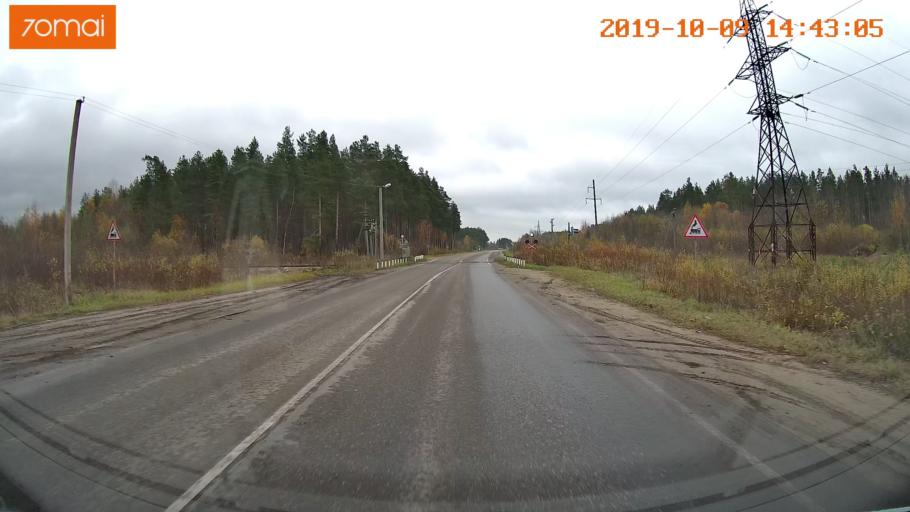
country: RU
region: Kostroma
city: Buy
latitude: 58.4585
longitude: 41.5414
